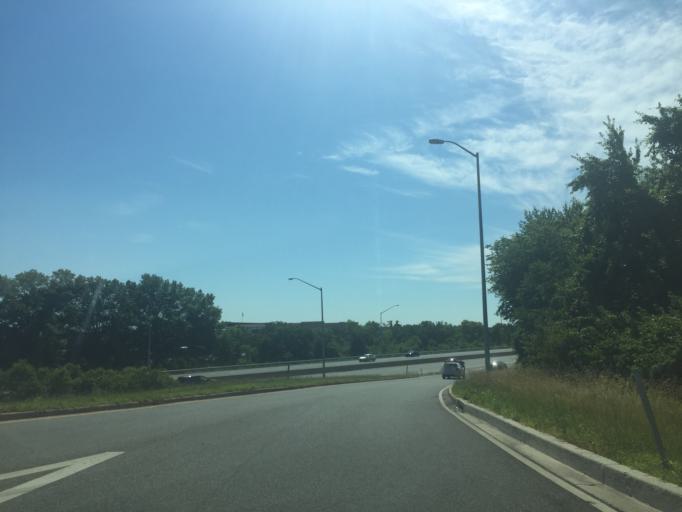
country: US
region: Maryland
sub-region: Baltimore County
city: Rossville
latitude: 39.3354
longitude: -76.4922
